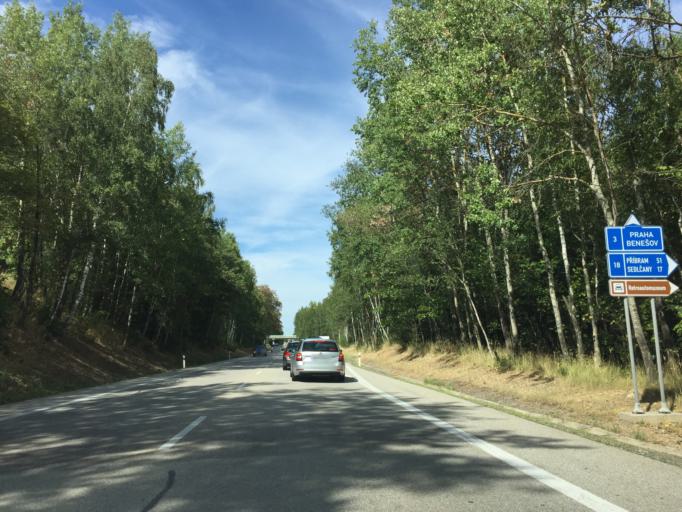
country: CZ
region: Central Bohemia
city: Votice
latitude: 49.6580
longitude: 14.6337
